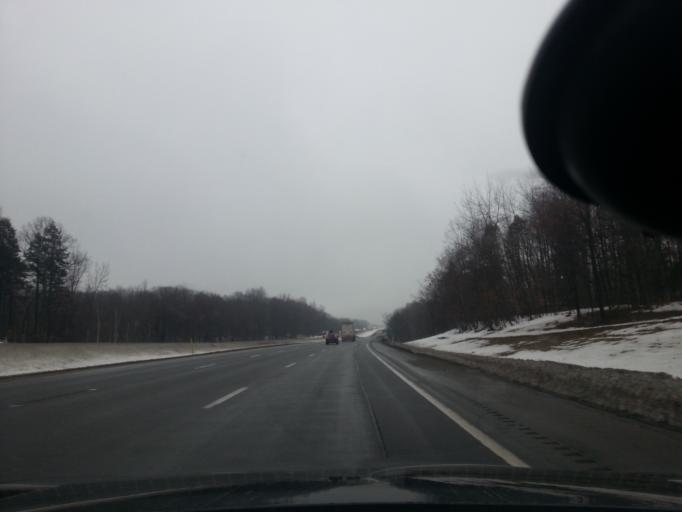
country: US
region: New York
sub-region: Jefferson County
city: Adams Center
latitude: 43.9000
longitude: -75.9850
